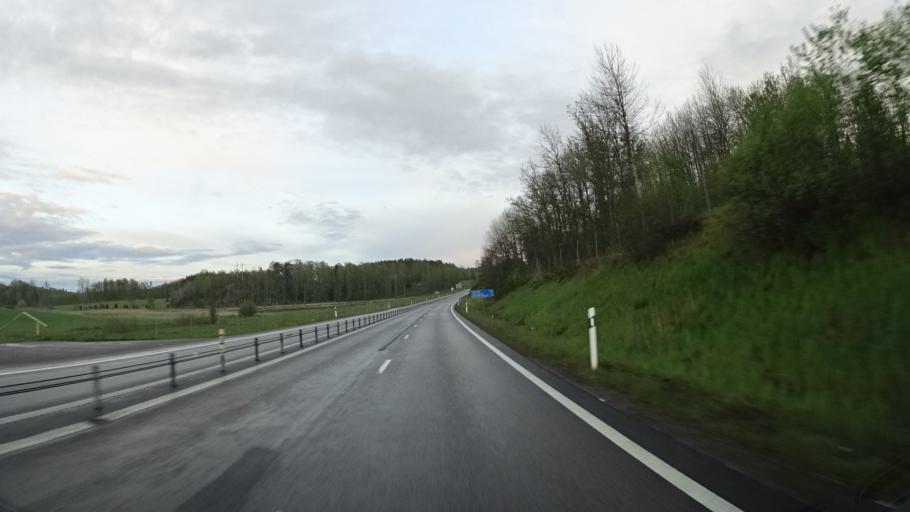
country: SE
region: OEstergoetland
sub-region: Valdemarsviks Kommun
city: Gusum
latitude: 58.2813
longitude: 16.5090
